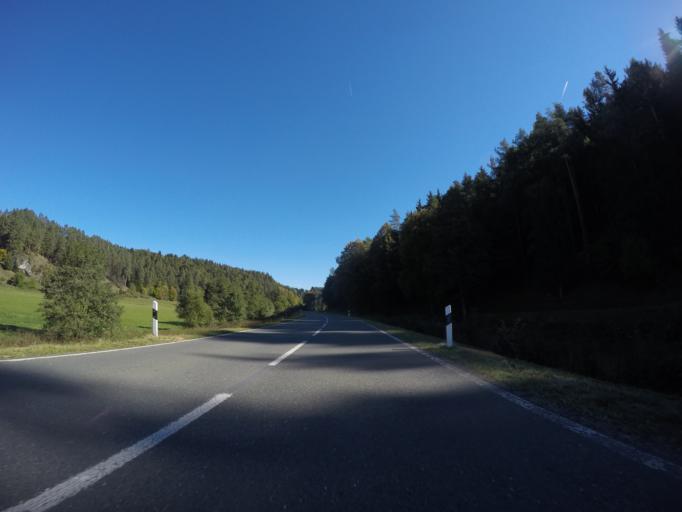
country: DE
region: Bavaria
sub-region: Upper Franconia
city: Waischenfeld
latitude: 49.8114
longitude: 11.3578
